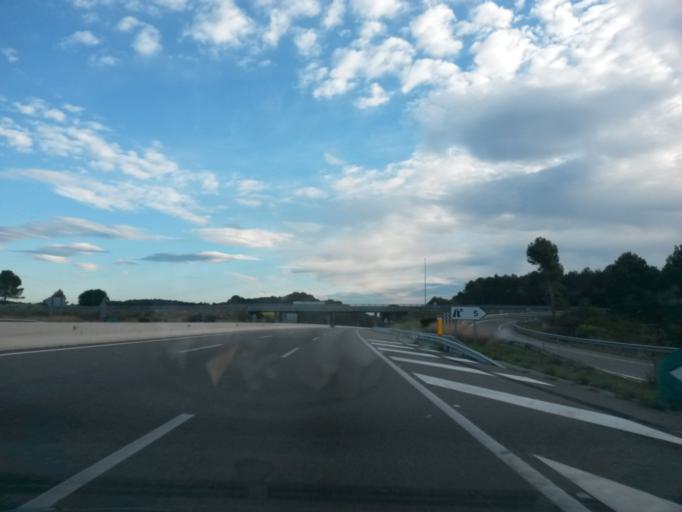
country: ES
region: Catalonia
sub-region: Provincia de Girona
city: Vilademuls
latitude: 42.1288
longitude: 2.9127
